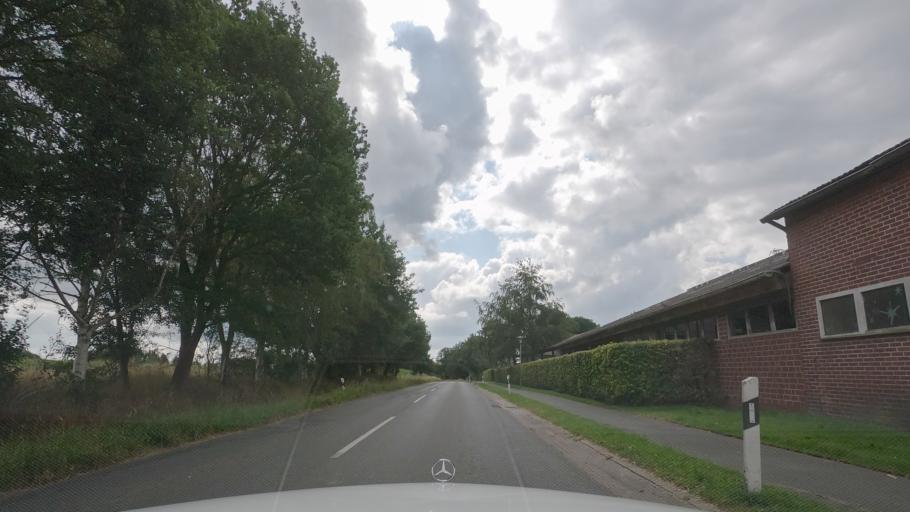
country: DE
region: Lower Saxony
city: Uthlede
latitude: 53.3072
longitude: 8.5807
